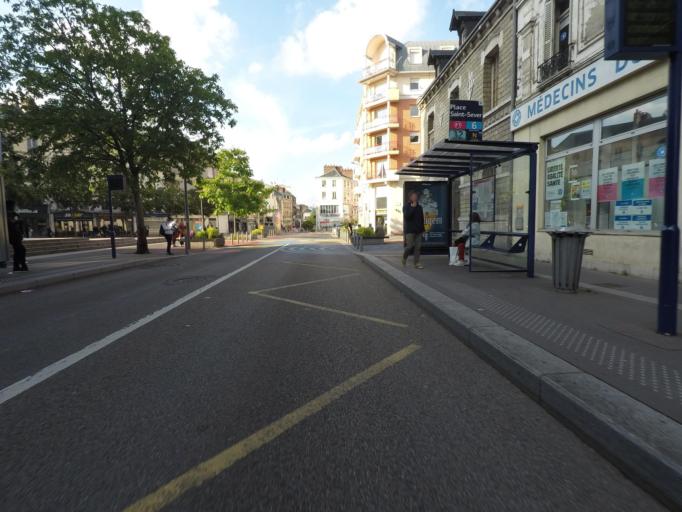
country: FR
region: Haute-Normandie
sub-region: Departement de la Seine-Maritime
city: Rouen
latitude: 49.4305
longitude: 1.0861
